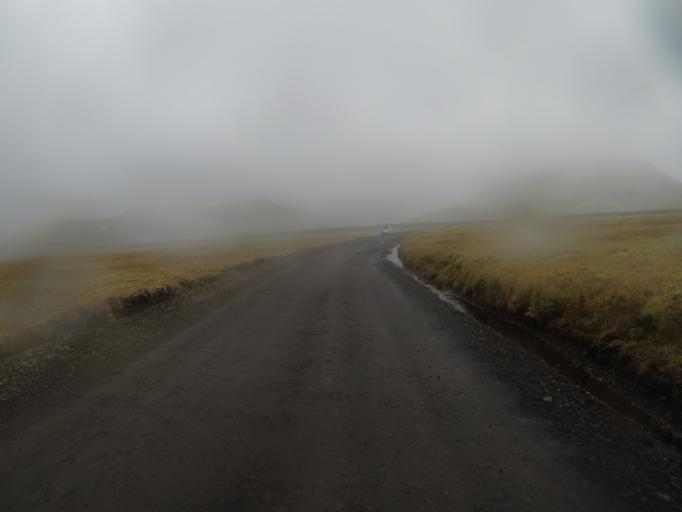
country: IS
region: South
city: Vestmannaeyjar
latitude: 63.9698
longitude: -18.8096
